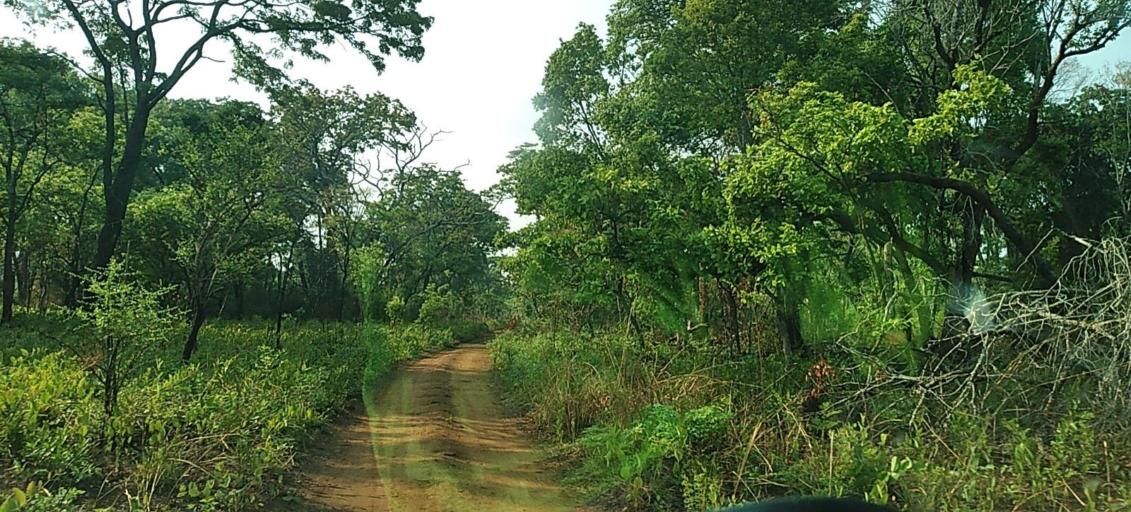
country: ZM
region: North-Western
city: Solwezi
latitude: -12.4077
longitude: 26.5882
